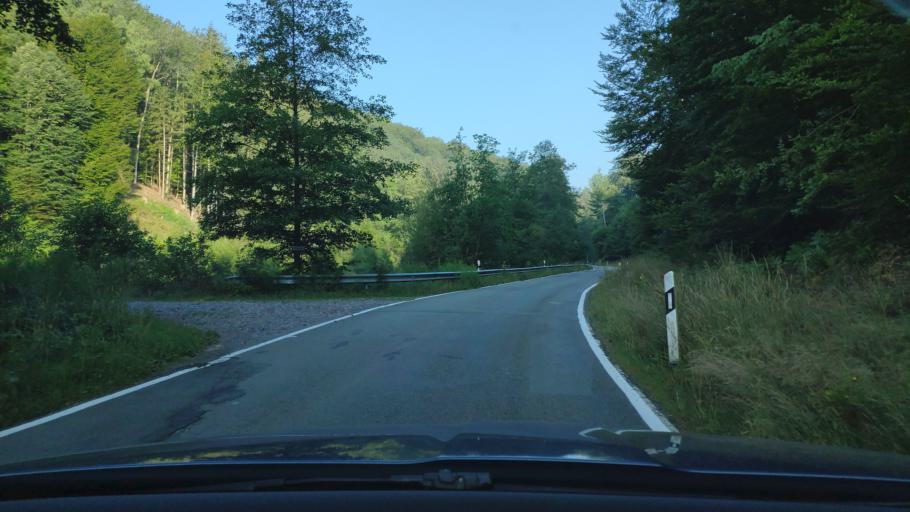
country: DE
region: Rheinland-Pfalz
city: Ludwigswinkel
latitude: 49.0964
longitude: 7.6315
